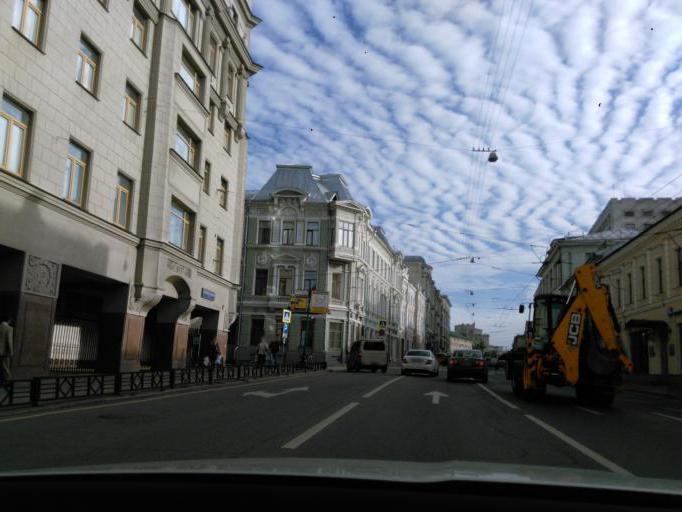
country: RU
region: Moscow
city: Moscow
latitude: 55.7627
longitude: 37.6286
